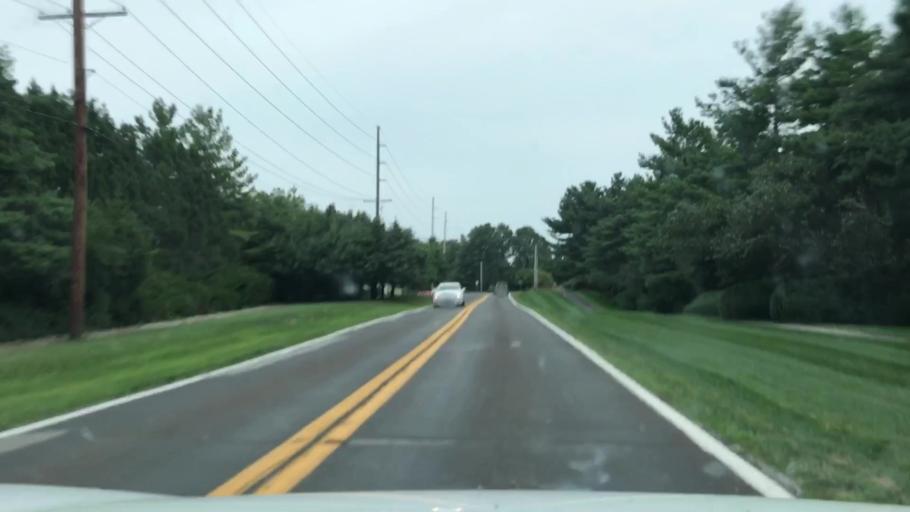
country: US
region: Missouri
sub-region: Saint Louis County
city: Clarkson Valley
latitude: 38.6298
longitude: -90.5984
